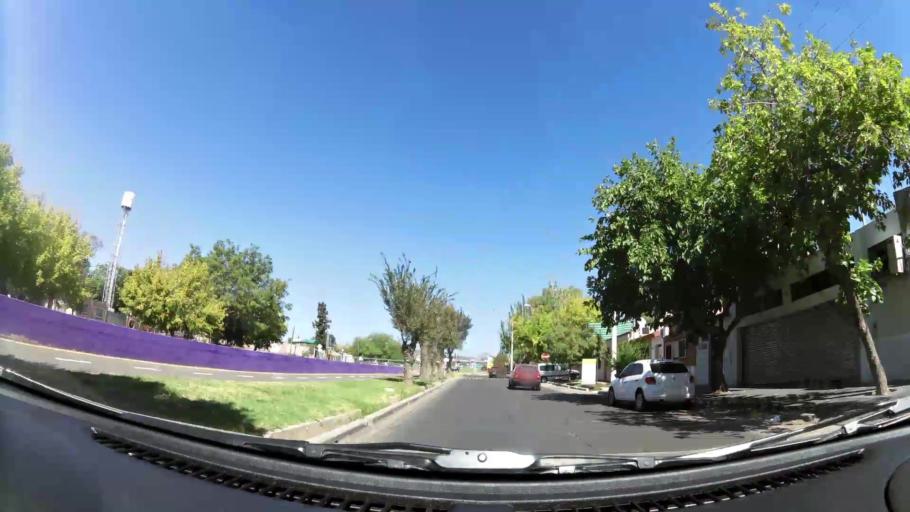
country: AR
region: Mendoza
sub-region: Departamento de Godoy Cruz
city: Godoy Cruz
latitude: -32.9229
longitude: -68.8615
